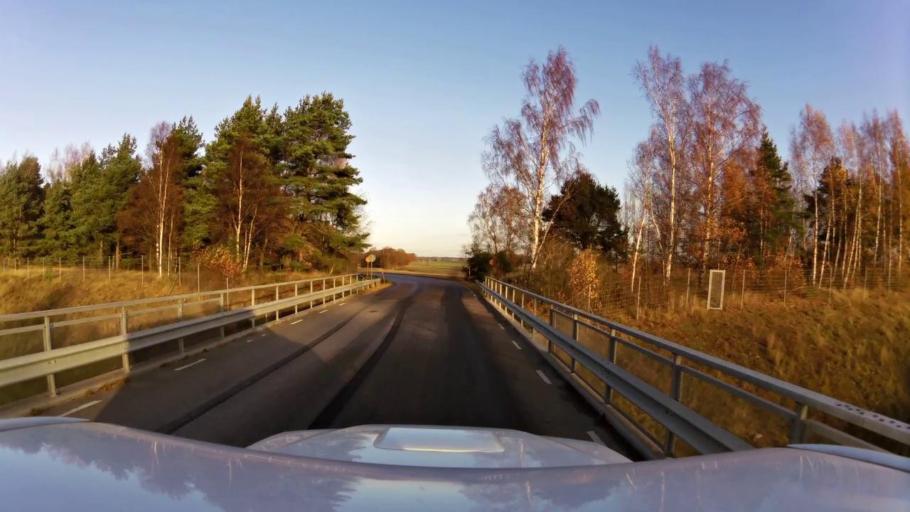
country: SE
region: OEstergoetland
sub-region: Linkopings Kommun
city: Ekangen
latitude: 58.4341
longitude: 15.6829
